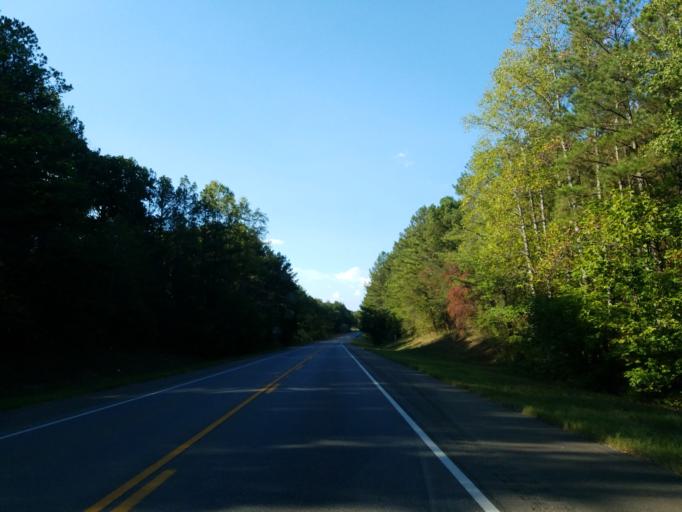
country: US
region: Georgia
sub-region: Murray County
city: Chatsworth
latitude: 34.5972
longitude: -84.7099
